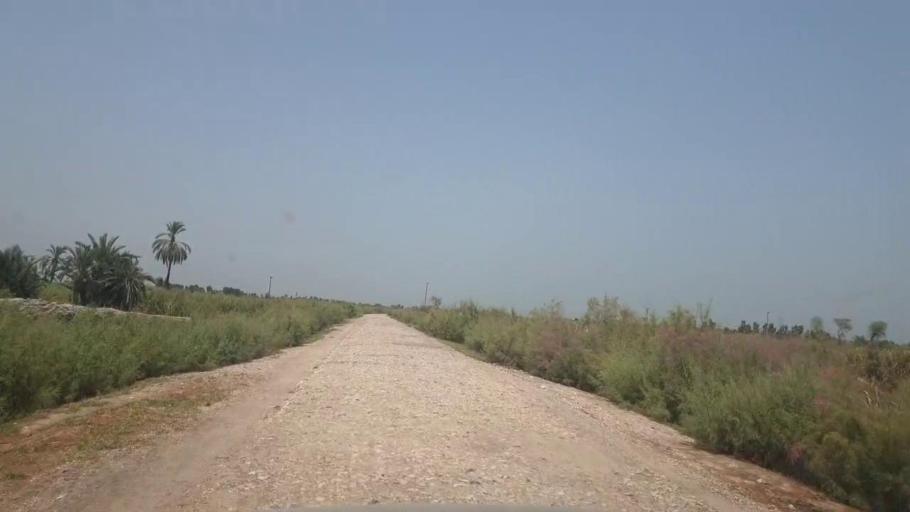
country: PK
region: Sindh
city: Lakhi
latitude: 27.8460
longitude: 68.6253
